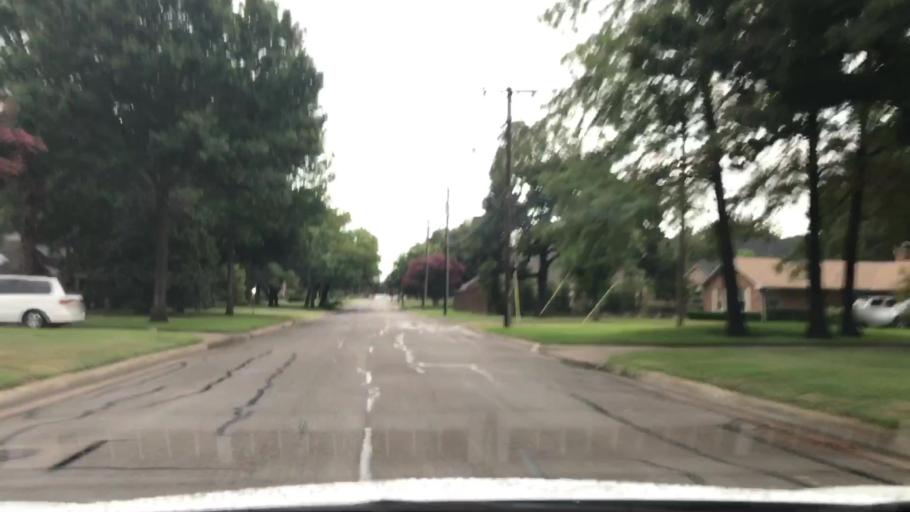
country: US
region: Texas
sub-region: Tarrant County
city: Arlington
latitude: 32.7542
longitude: -97.1258
